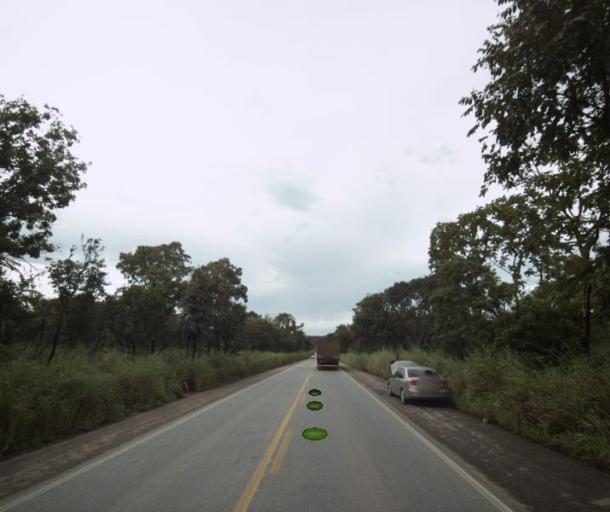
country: BR
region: Goias
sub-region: Porangatu
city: Porangatu
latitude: -13.6189
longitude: -49.0425
